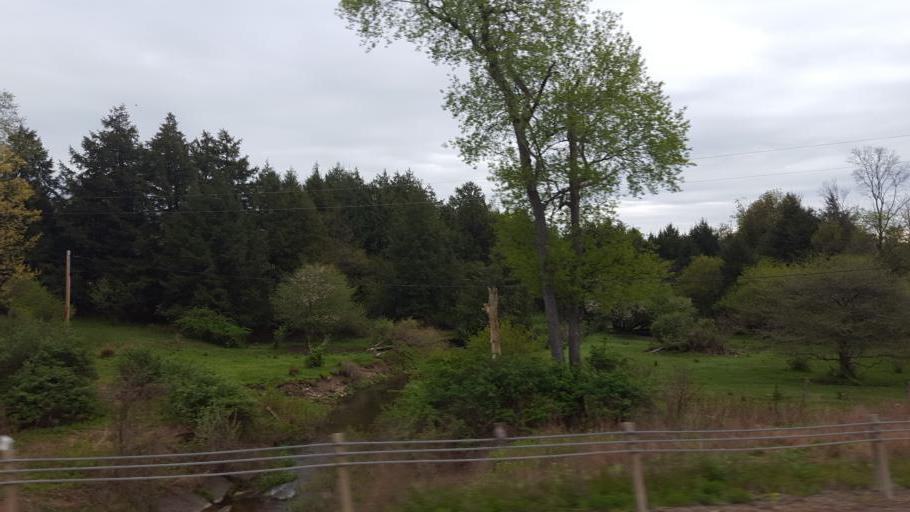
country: US
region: Pennsylvania
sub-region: Tioga County
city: Westfield
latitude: 42.0070
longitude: -77.4805
